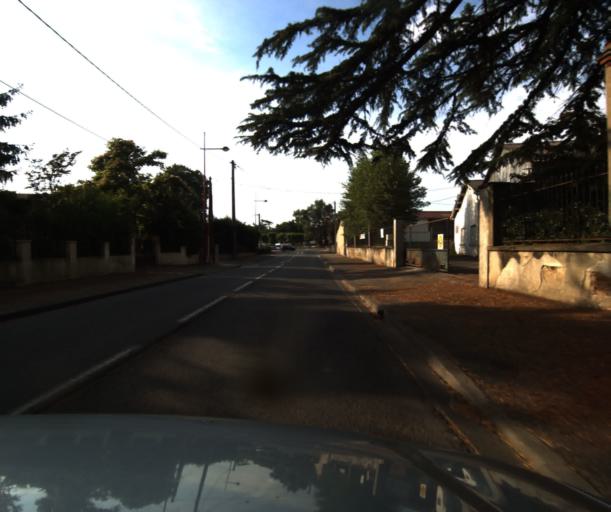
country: FR
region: Midi-Pyrenees
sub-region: Departement du Tarn-et-Garonne
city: Castelsarrasin
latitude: 44.0345
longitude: 1.1063
